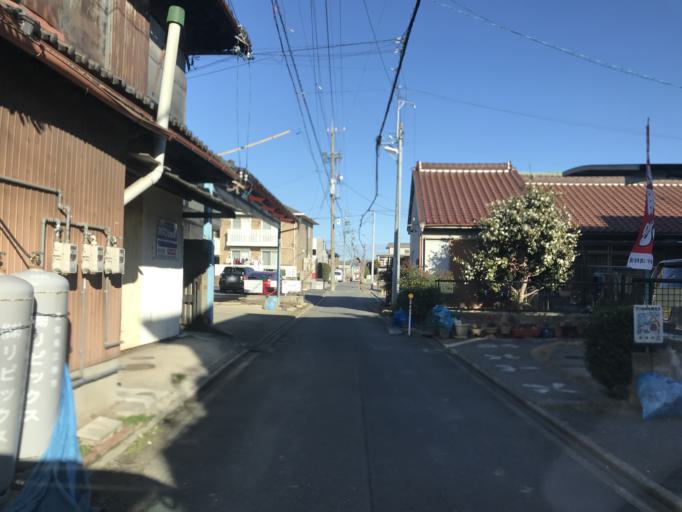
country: JP
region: Aichi
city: Nagoya-shi
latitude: 35.2030
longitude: 136.8419
